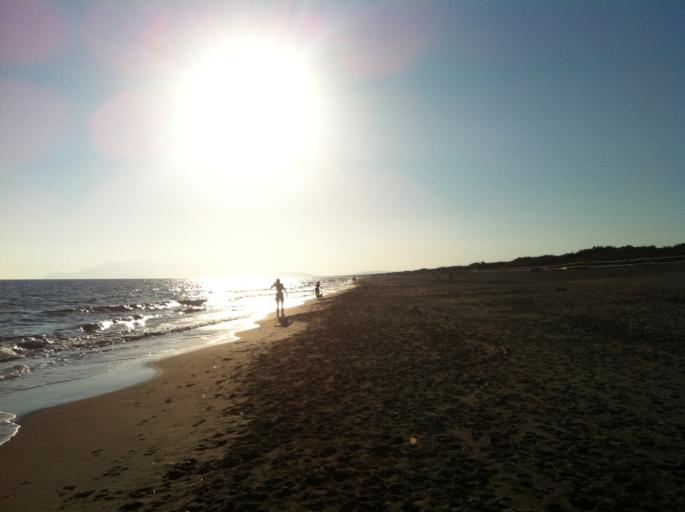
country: IT
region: Latium
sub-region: Provincia di Viterbo
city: Pescia Romana
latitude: 42.3809
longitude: 11.4390
